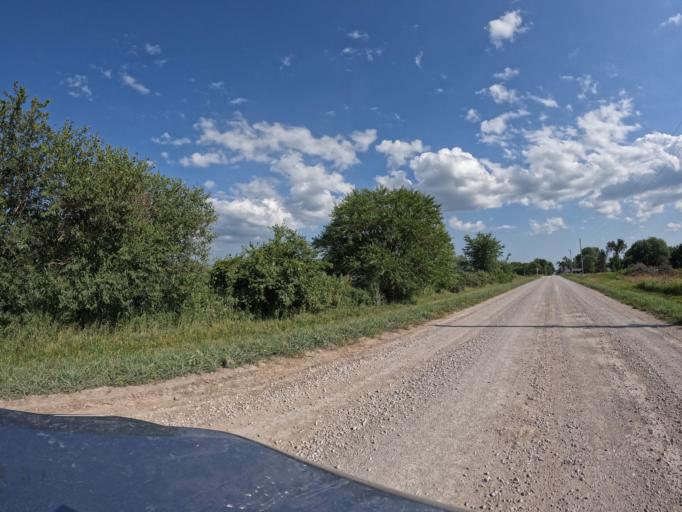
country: US
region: Iowa
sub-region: Appanoose County
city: Centerville
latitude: 40.7216
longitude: -93.0299
